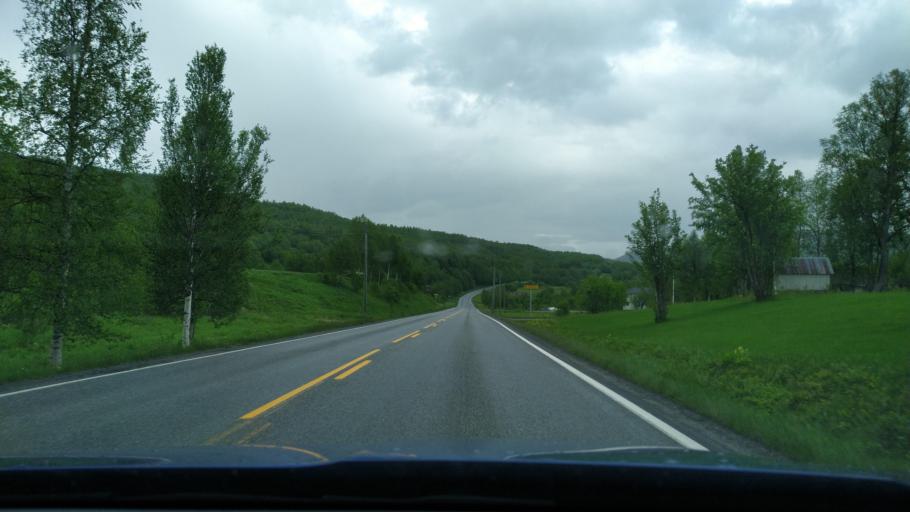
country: NO
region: Troms
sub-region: Malselv
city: Moen
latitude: 69.1129
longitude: 18.8708
